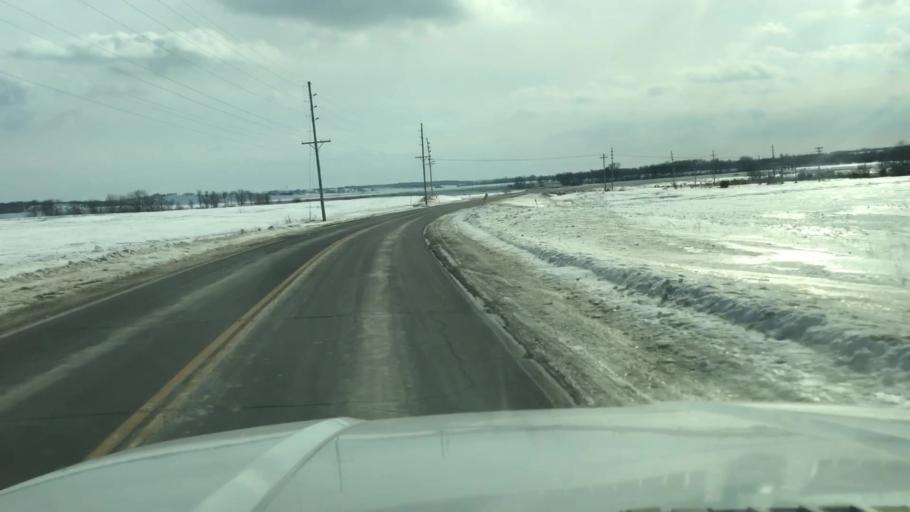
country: US
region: Missouri
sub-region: Gentry County
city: Stanberry
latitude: 40.3453
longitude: -94.6734
